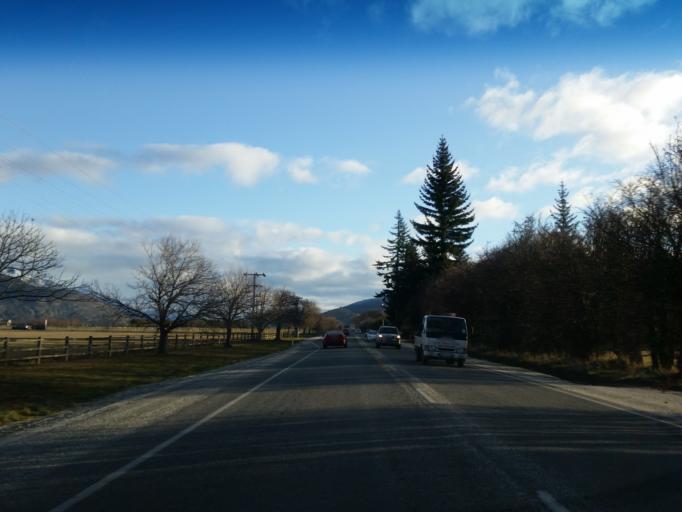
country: NZ
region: Otago
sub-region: Queenstown-Lakes District
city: Arrowtown
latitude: -44.9970
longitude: 168.7849
